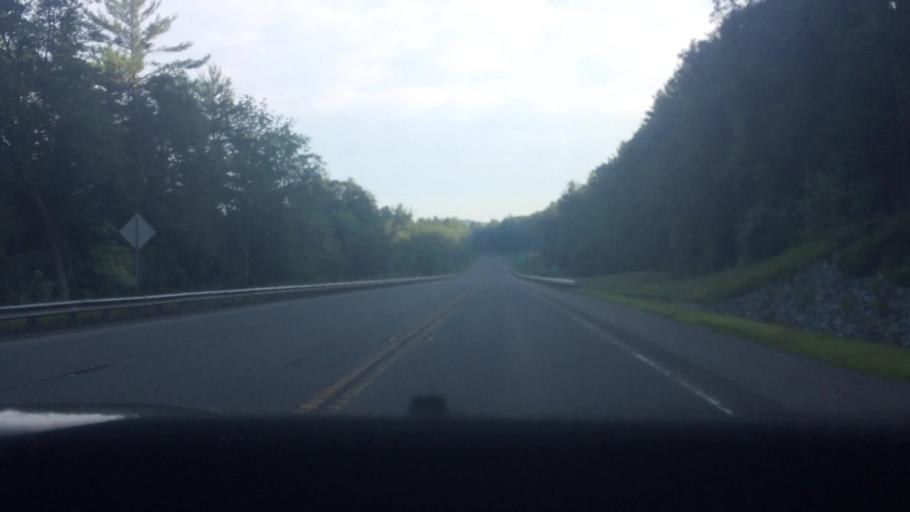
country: US
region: Massachusetts
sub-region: Franklin County
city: Orange
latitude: 42.5785
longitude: -72.3247
